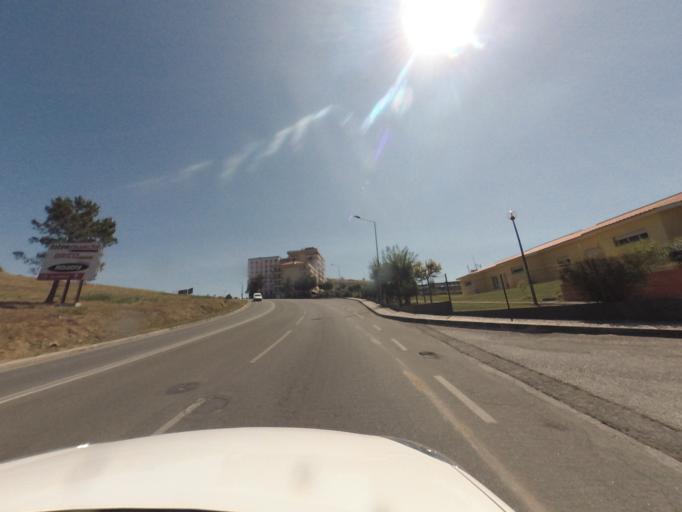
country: PT
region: Leiria
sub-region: Alcobaca
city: Alcobaca
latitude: 39.5569
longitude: -8.9766
